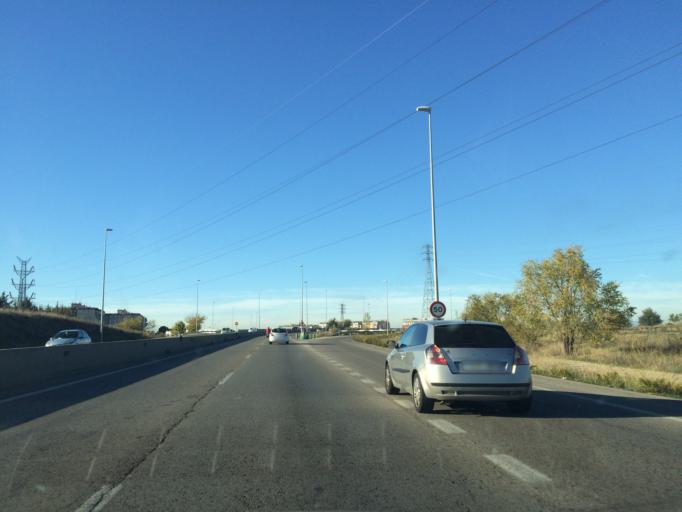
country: ES
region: Madrid
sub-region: Provincia de Madrid
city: Mostoles
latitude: 40.3300
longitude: -3.8511
